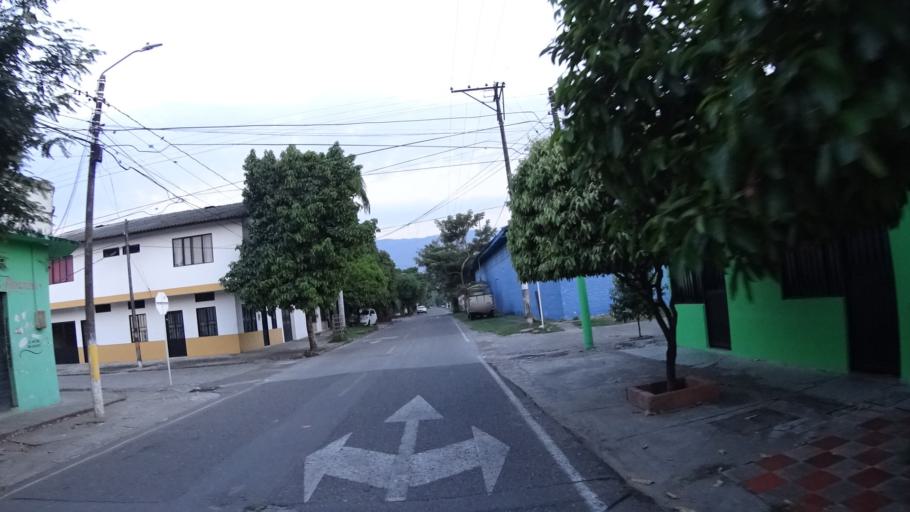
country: CO
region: Caldas
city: La Dorada
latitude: 5.4473
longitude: -74.6621
